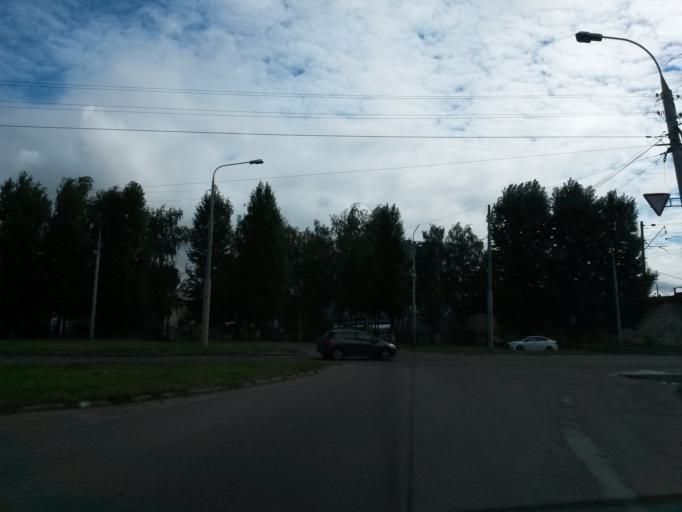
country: RU
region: Jaroslavl
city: Yaroslavl
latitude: 57.6460
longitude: 39.8798
